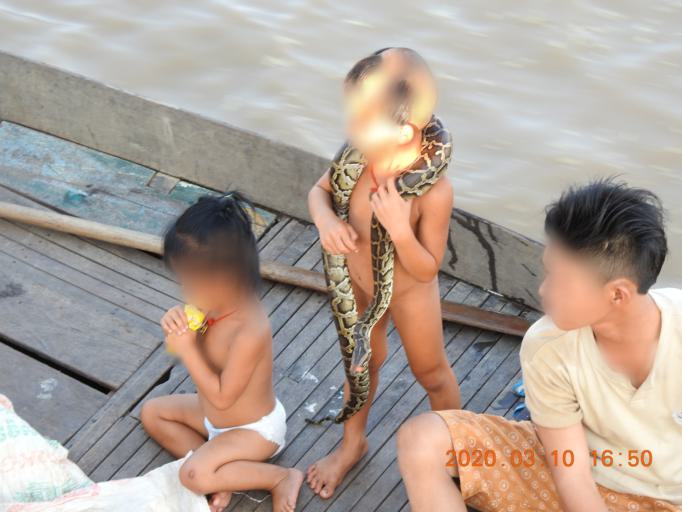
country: KH
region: Siem Reap
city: Siem Reap
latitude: 13.2239
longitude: 103.8260
